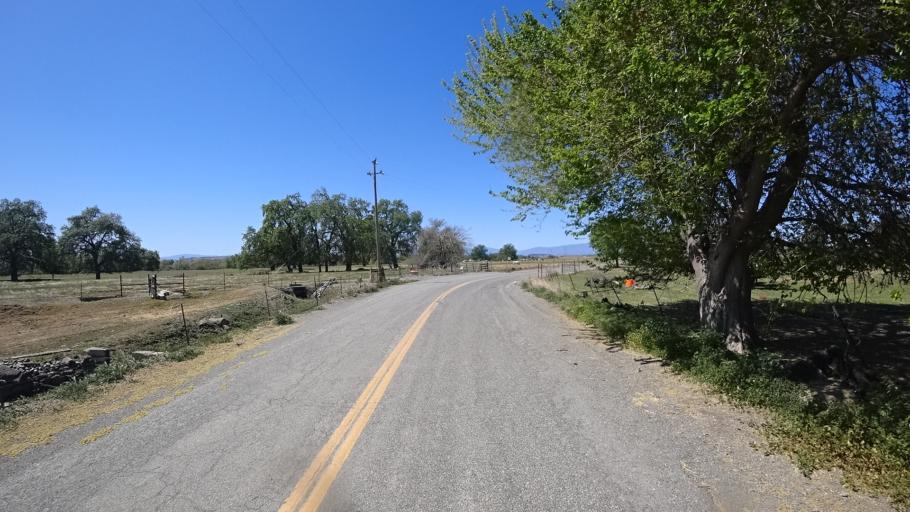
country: US
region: California
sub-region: Glenn County
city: Orland
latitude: 39.7954
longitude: -122.2503
